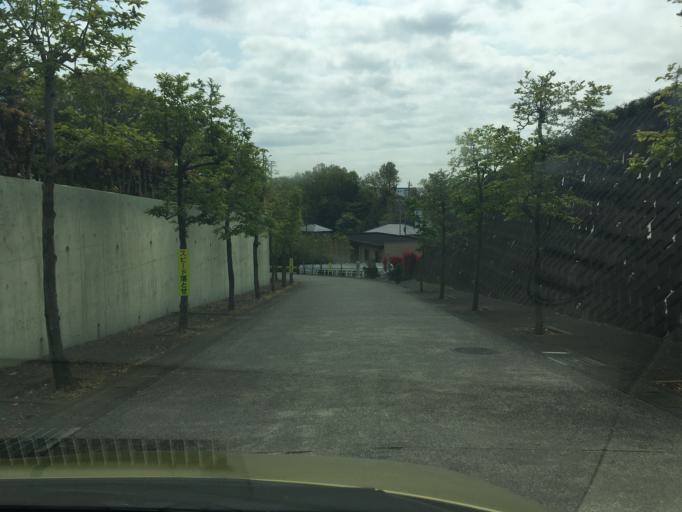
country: JP
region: Kanagawa
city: Zama
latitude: 35.5354
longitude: 139.3174
